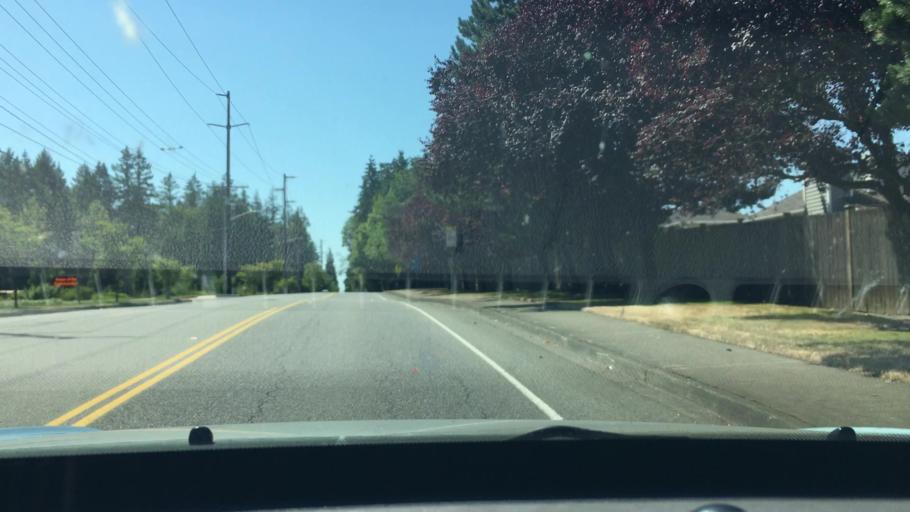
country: US
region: Washington
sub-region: King County
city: Newport
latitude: 47.5418
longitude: -122.1857
